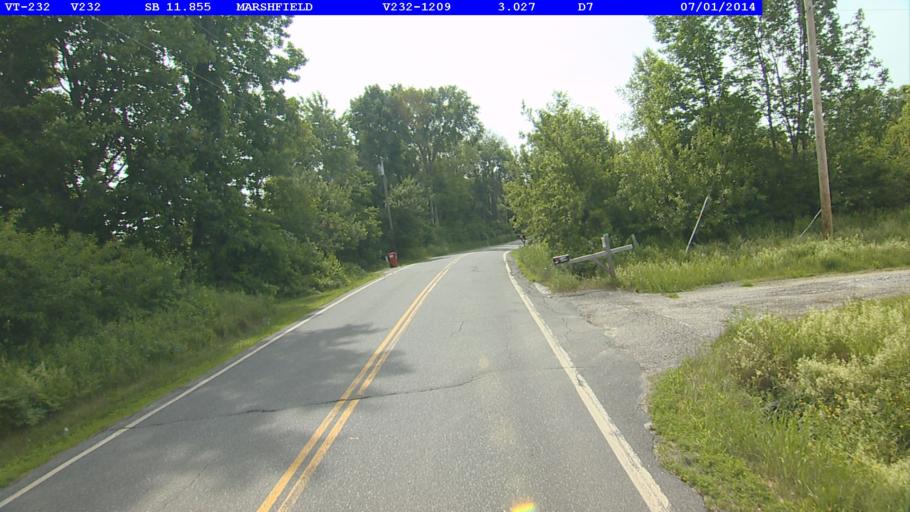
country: US
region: Vermont
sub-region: Caledonia County
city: Hardwick
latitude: 44.3494
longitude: -72.3017
